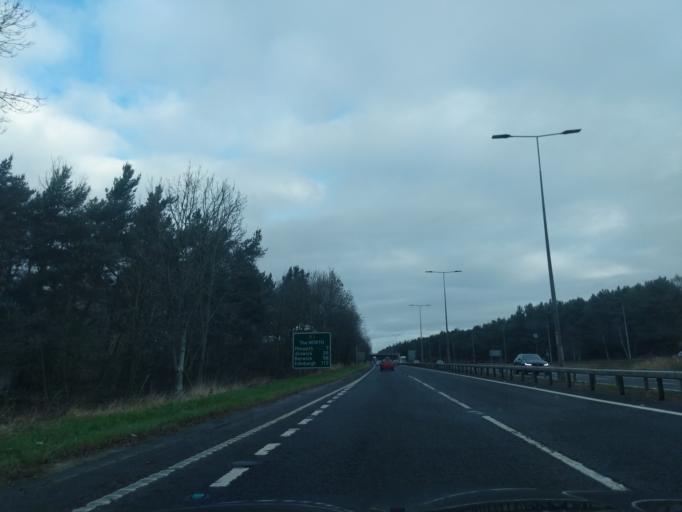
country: GB
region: England
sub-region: Newcastle upon Tyne
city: Hazlerigg
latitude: 55.0656
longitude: -1.6378
